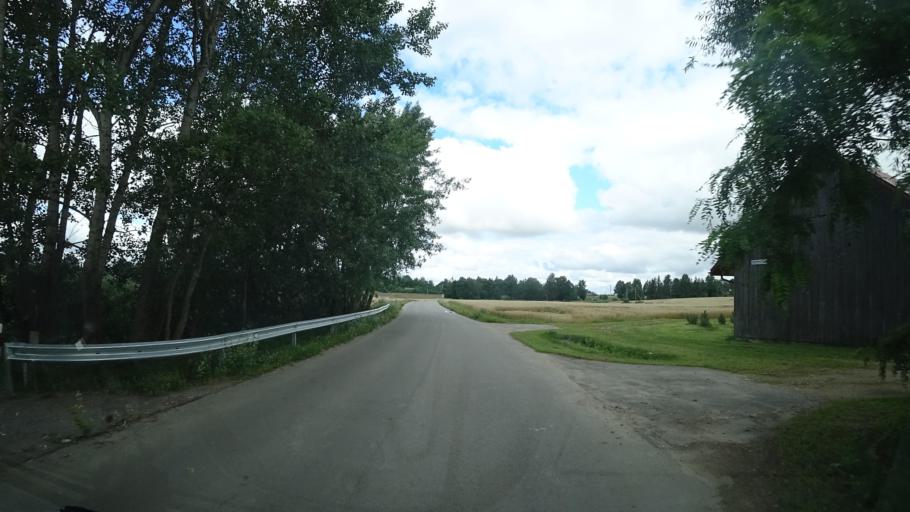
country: LT
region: Marijampoles apskritis
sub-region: Marijampole Municipality
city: Marijampole
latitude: 54.5191
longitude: 23.3217
